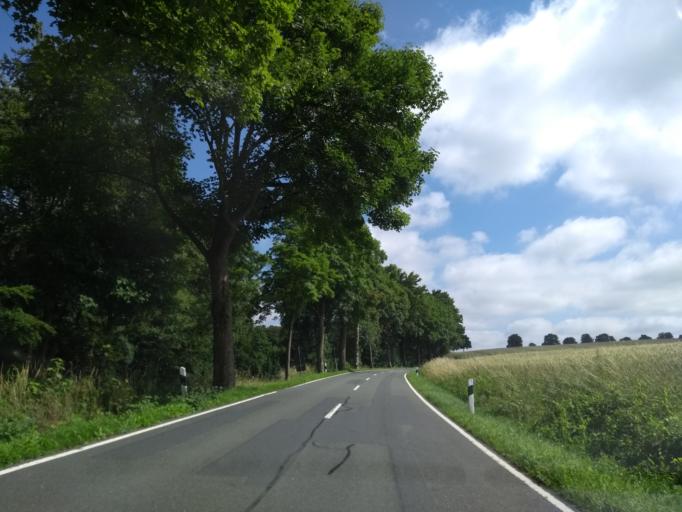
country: DE
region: Lower Saxony
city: Bad Pyrmont
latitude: 51.9658
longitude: 9.3048
